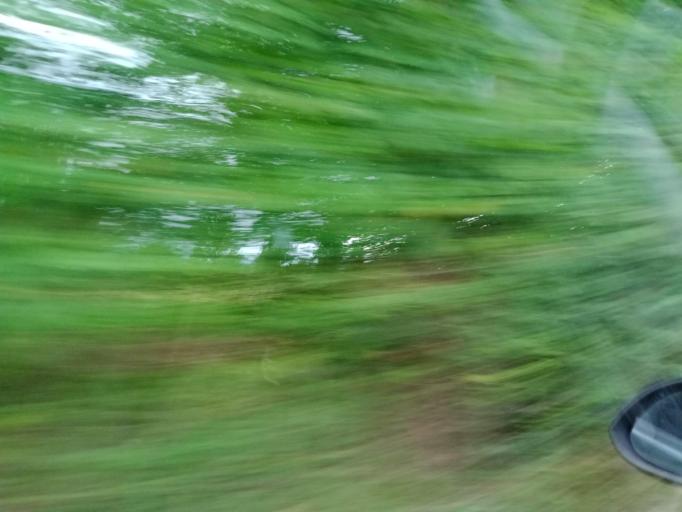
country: IE
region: Leinster
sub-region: Laois
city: Mountmellick
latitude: 53.1143
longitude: -7.3596
